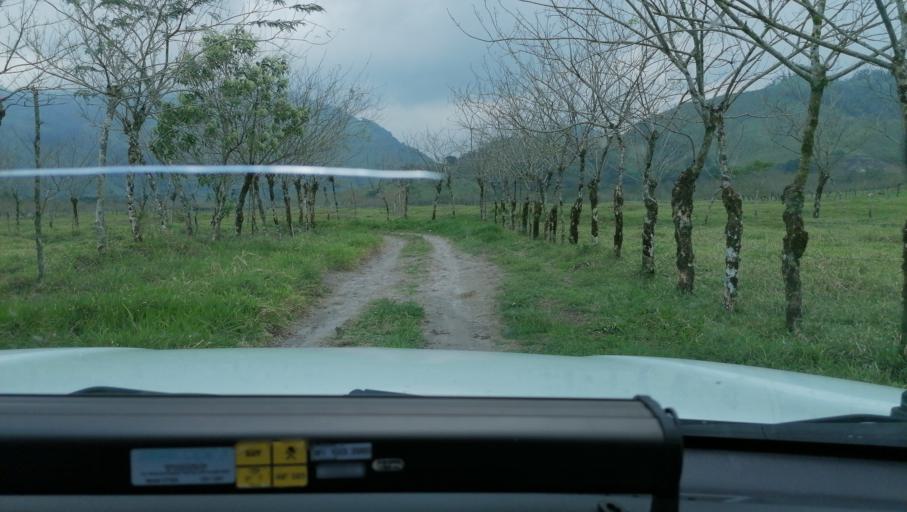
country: MX
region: Chiapas
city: Ixtacomitan
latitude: 17.3650
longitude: -93.1882
